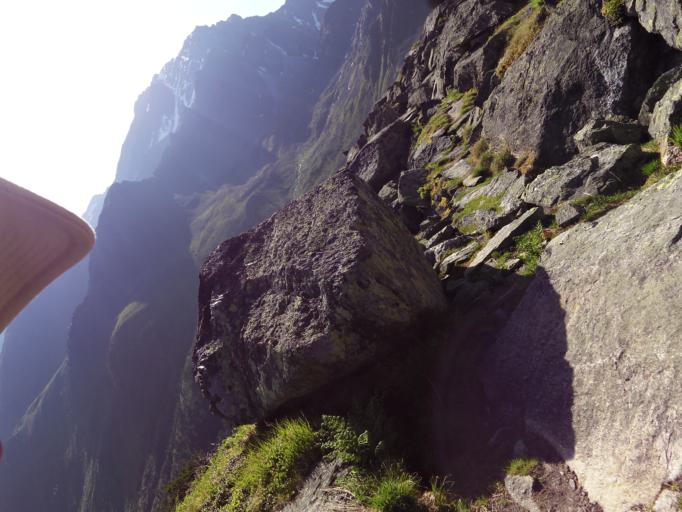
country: AT
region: Tyrol
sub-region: Politischer Bezirk Innsbruck Land
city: Gries im Sellrain
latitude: 47.0870
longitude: 11.1805
